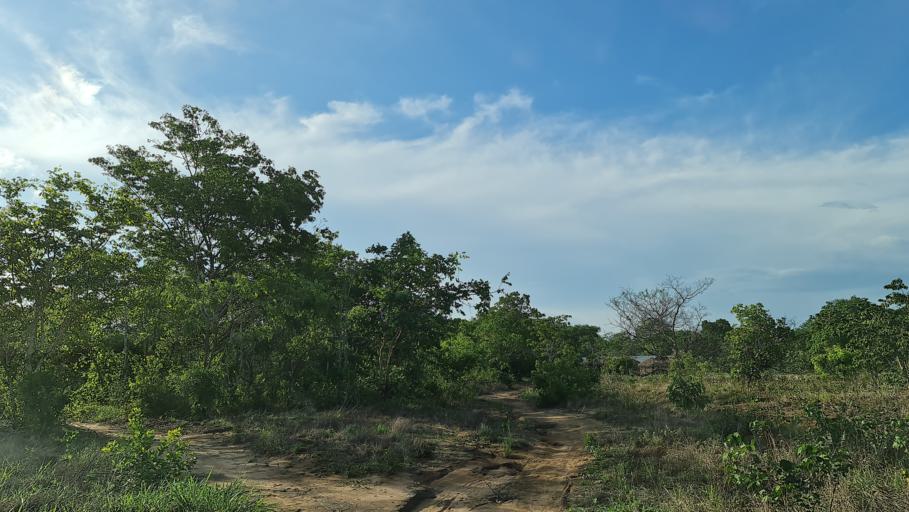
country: MZ
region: Zambezia
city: Quelimane
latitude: -17.1921
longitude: 37.4135
